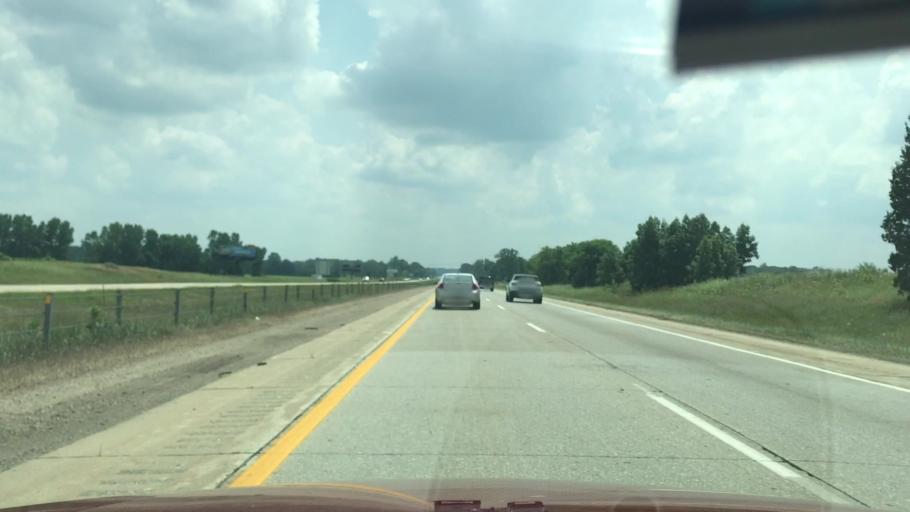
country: US
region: Michigan
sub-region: Allegan County
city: Plainwell
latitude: 42.4331
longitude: -85.6611
